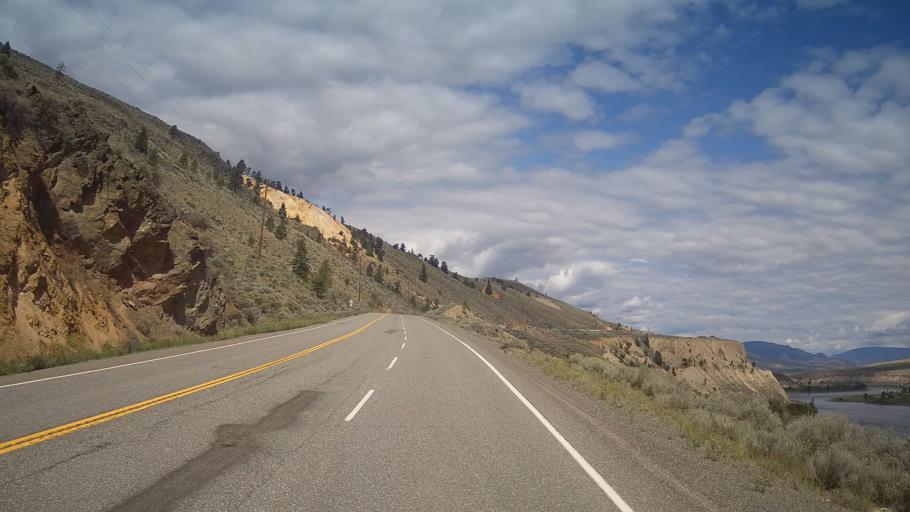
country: CA
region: British Columbia
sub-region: Thompson-Nicola Regional District
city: Ashcroft
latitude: 50.5525
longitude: -121.2973
